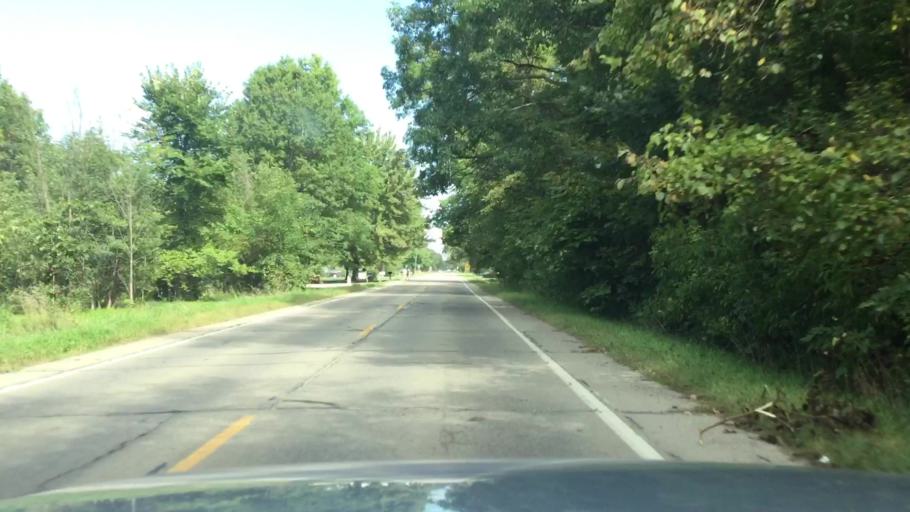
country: US
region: Michigan
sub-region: Wayne County
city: Belleville
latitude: 42.1651
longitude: -83.4825
